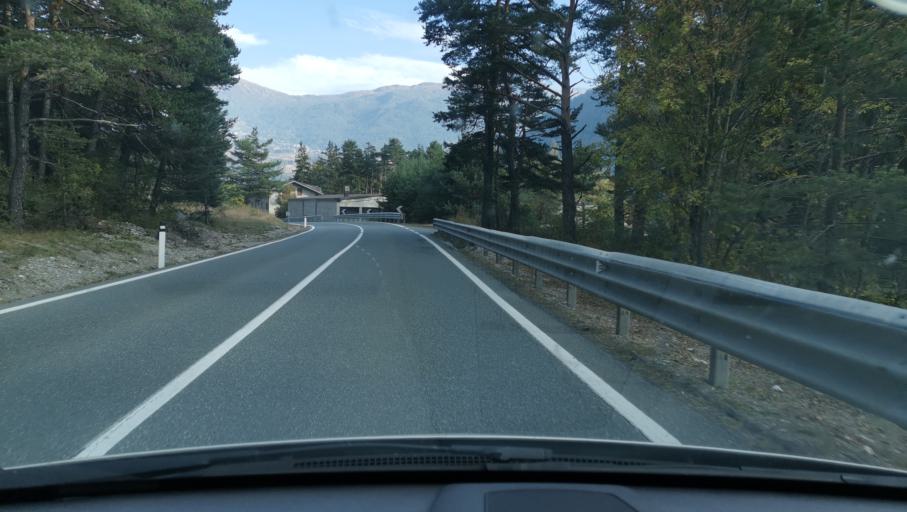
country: IT
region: Piedmont
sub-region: Provincia di Torino
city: Oulx
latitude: 45.0425
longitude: 6.8074
